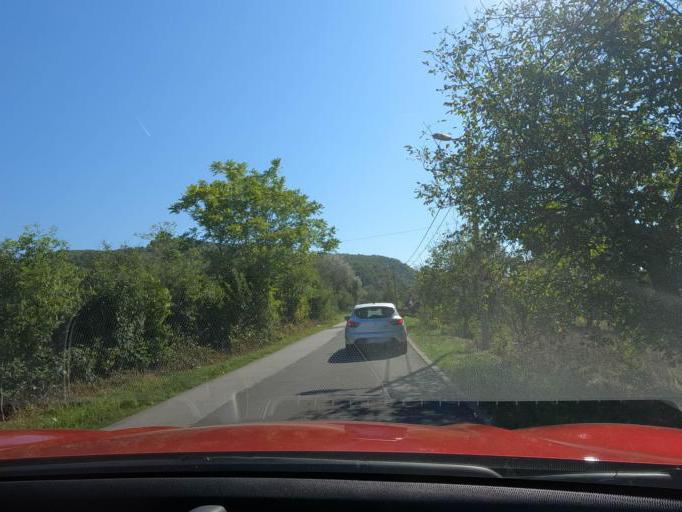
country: RS
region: Central Serbia
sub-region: Raski Okrug
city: Kraljevo
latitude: 43.7393
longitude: 20.7357
